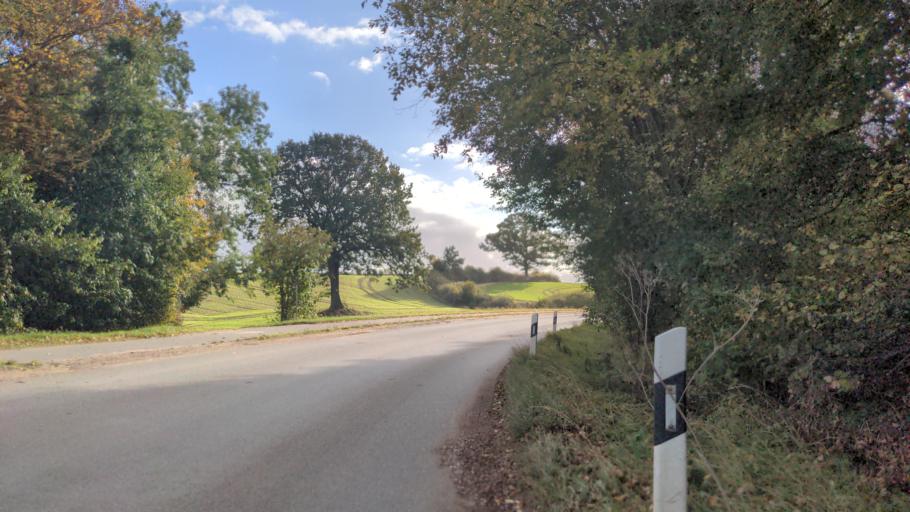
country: DE
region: Schleswig-Holstein
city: Bosdorf
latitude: 54.1297
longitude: 10.4678
